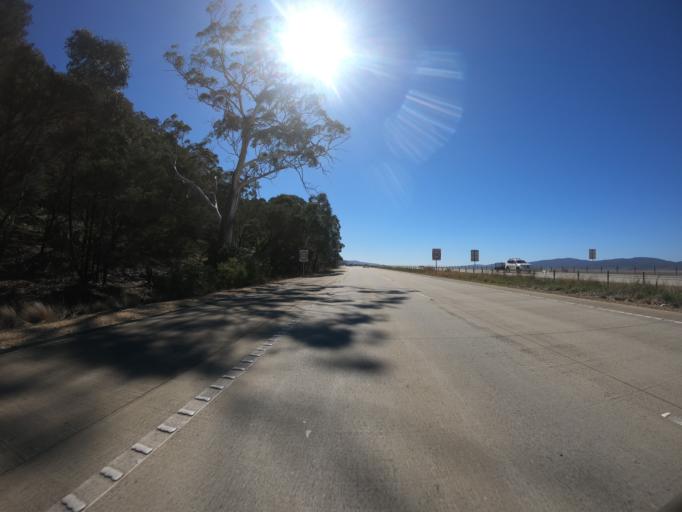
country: AU
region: New South Wales
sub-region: Yass Valley
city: Gundaroo
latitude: -35.0445
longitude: 149.3767
